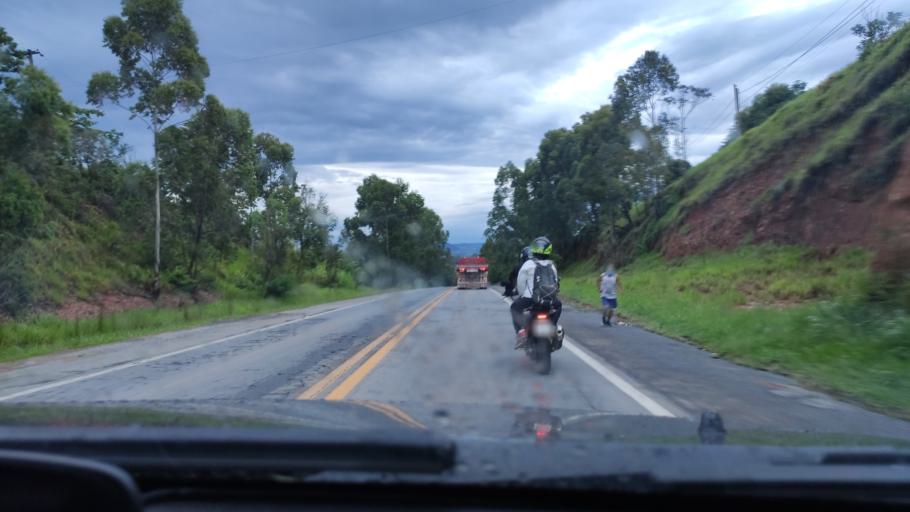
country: BR
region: Sao Paulo
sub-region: Socorro
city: Socorro
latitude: -22.7482
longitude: -46.5634
